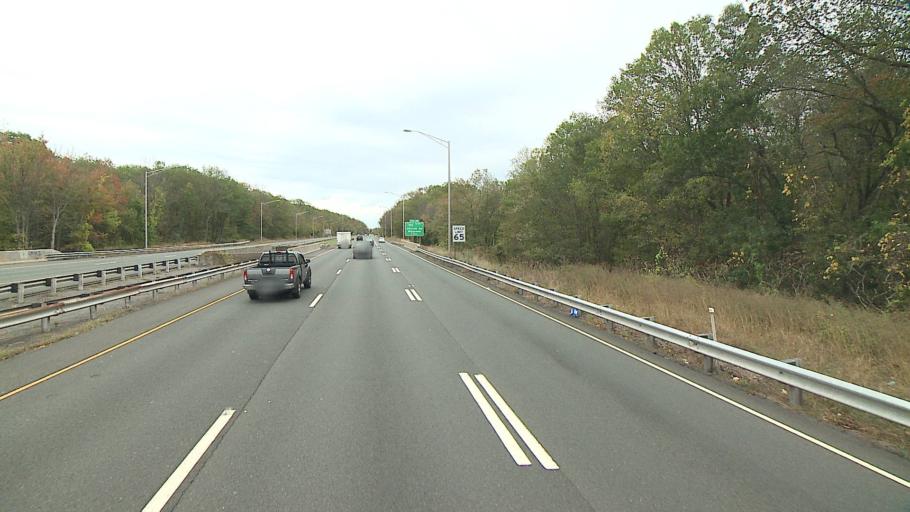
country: US
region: Connecticut
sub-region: Middlesex County
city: Middletown
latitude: 41.5278
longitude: -72.6134
